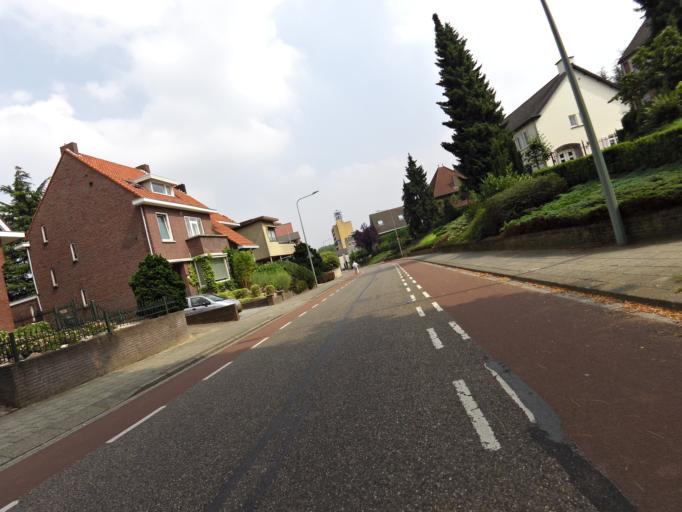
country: NL
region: Limburg
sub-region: Gemeente Brunssum
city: Brunssum
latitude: 50.9442
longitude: 5.9675
